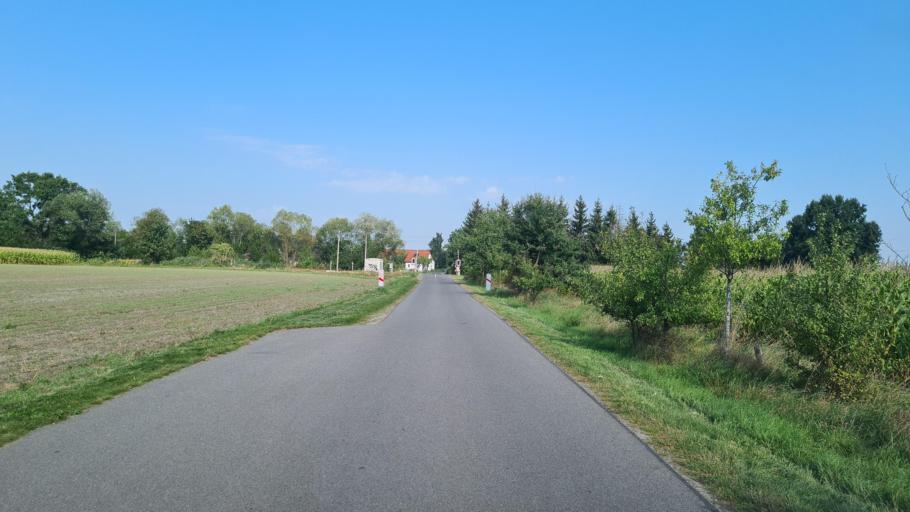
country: DE
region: Brandenburg
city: Kolkwitz
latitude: 51.7431
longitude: 14.2096
